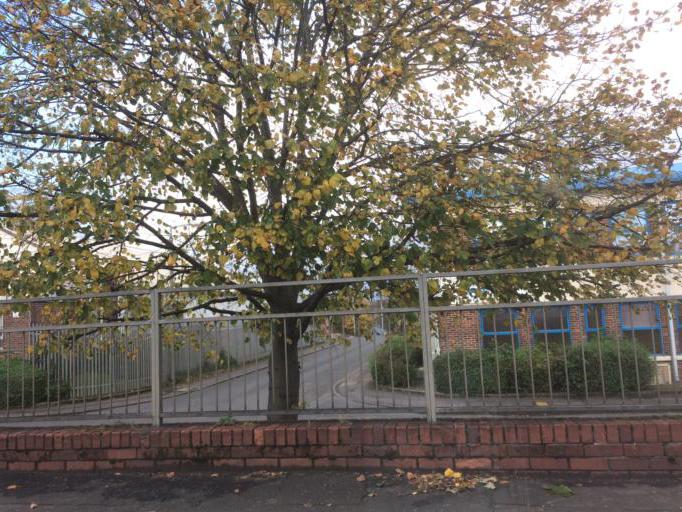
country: GB
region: Scotland
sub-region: East Renfrewshire
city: Newton Mearns
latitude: 55.8018
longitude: -4.3285
